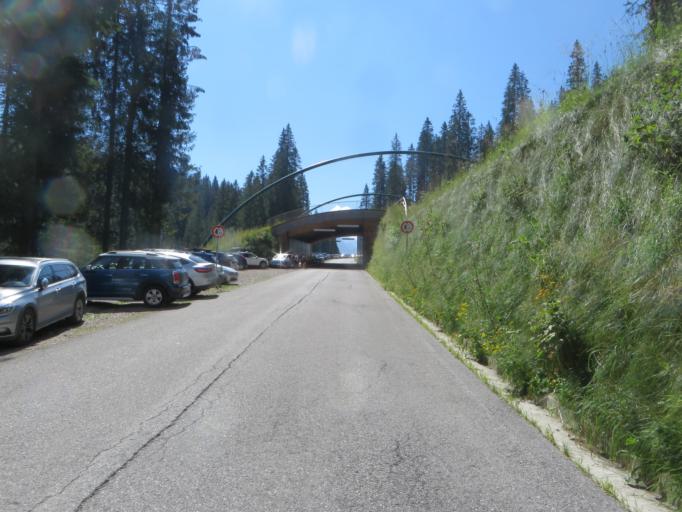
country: IT
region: Trentino-Alto Adige
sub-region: Provincia di Trento
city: Mezzana
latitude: 46.2339
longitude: 10.8152
